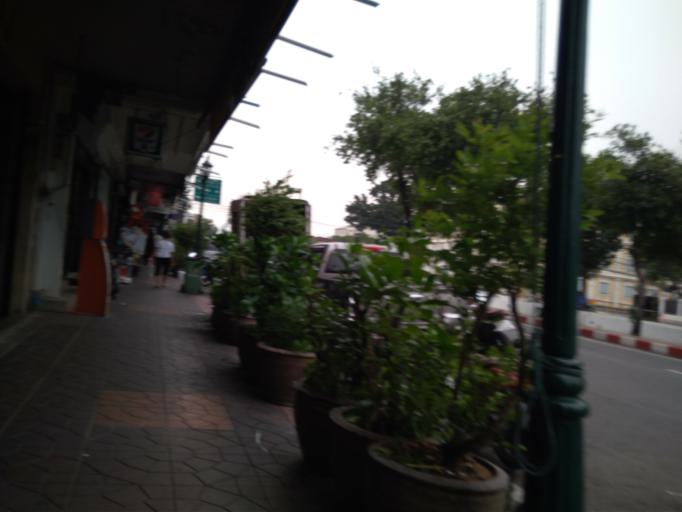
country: TH
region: Bangkok
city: Bangkok
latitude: 13.7530
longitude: 100.4962
